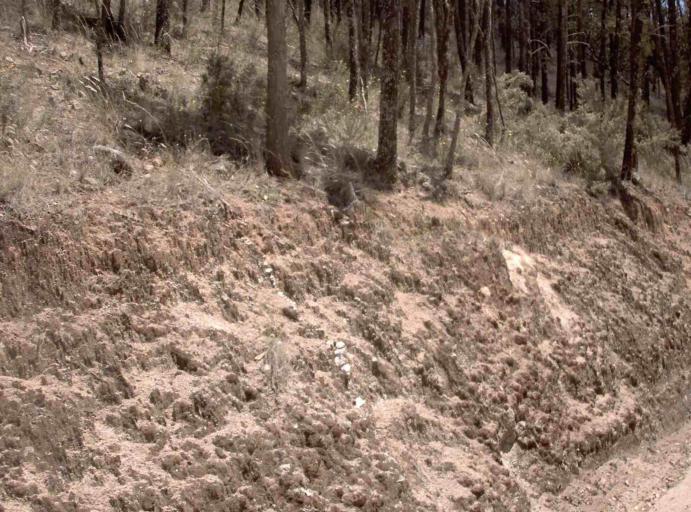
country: AU
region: New South Wales
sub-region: Snowy River
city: Jindabyne
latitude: -36.9080
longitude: 148.4161
